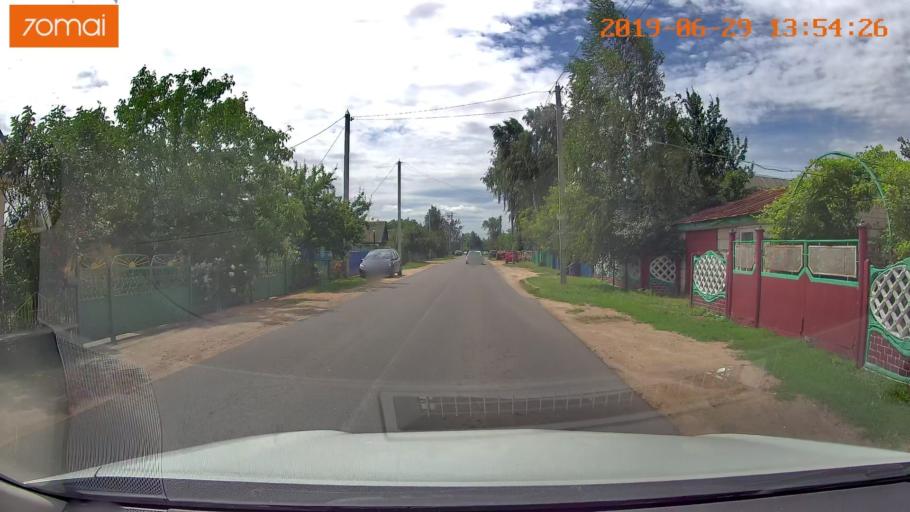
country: BY
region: Minsk
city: Slutsk
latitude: 52.9849
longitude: 27.5324
